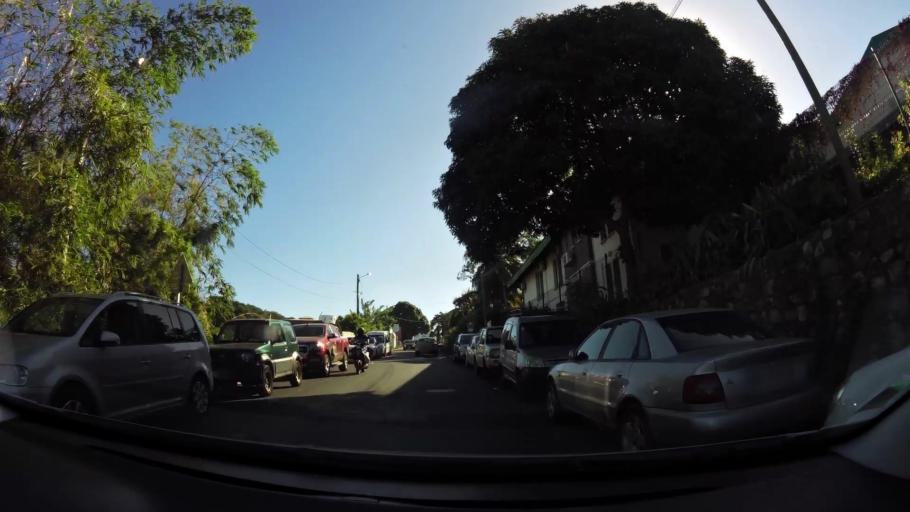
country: YT
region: Mamoudzou
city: Mamoudzou
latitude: -12.7778
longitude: 45.2301
